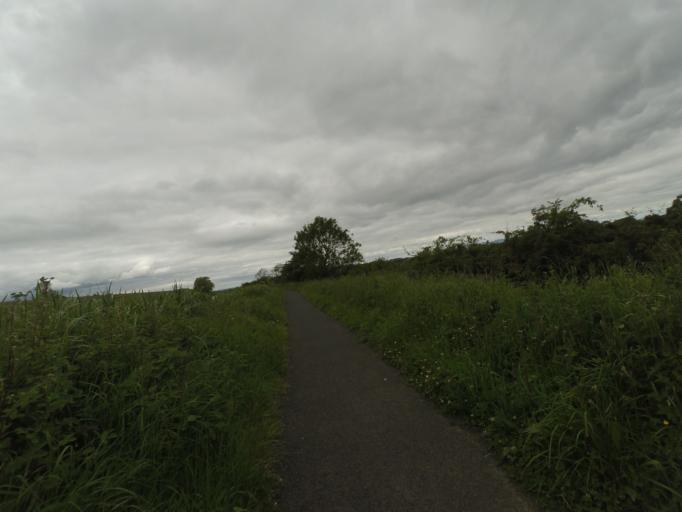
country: GB
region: Scotland
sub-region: West Lothian
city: Linlithgow
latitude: 55.9769
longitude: -3.5396
